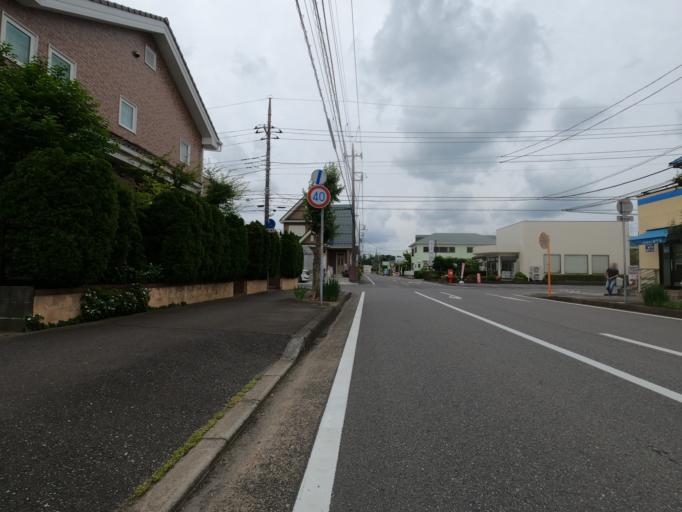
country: JP
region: Ibaraki
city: Moriya
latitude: 35.9620
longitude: 139.9623
